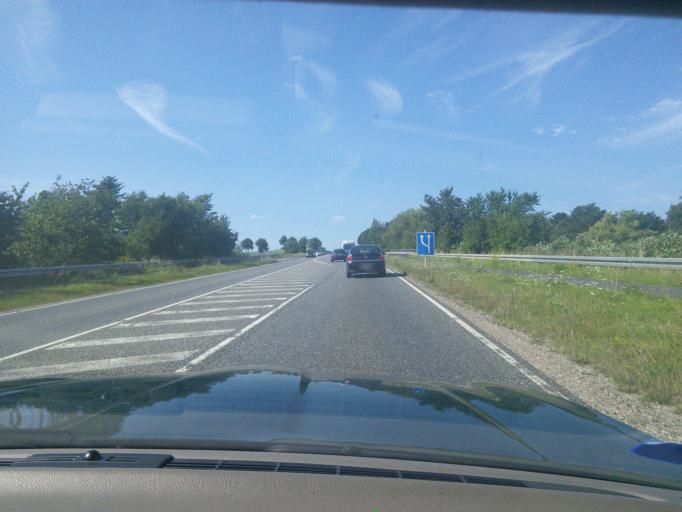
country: DK
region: Capital Region
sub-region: Halsnaes Kommune
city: Frederiksvaerk
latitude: 55.9539
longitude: 12.0400
